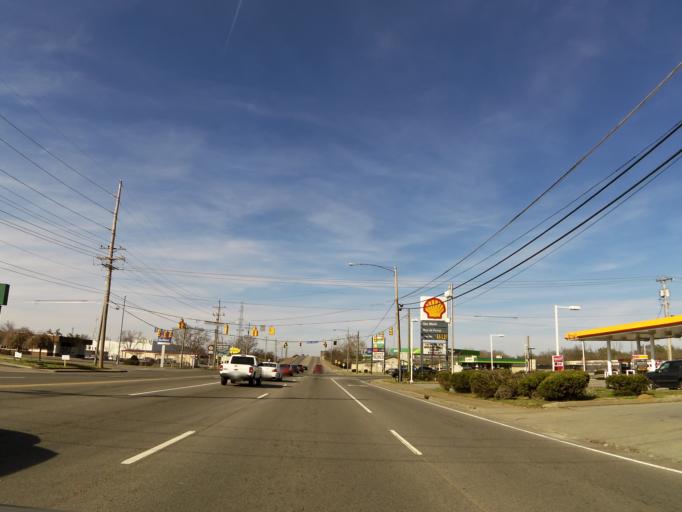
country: US
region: Tennessee
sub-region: Rutherford County
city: Murfreesboro
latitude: 35.8268
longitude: -86.3943
